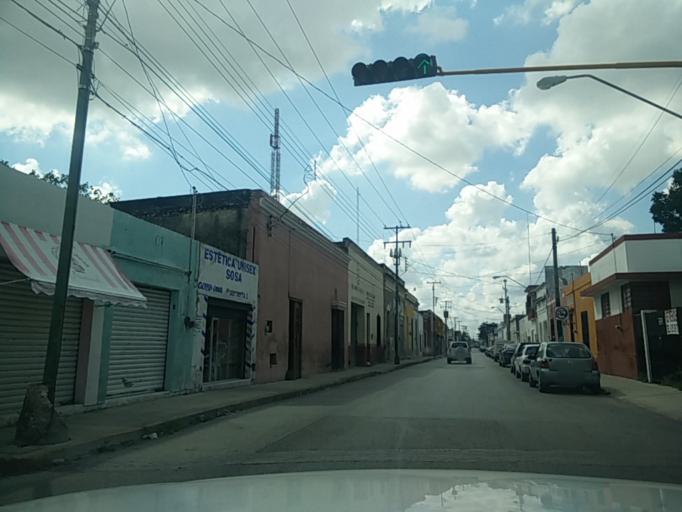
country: MX
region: Yucatan
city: Merida
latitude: 20.9808
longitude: -89.6221
